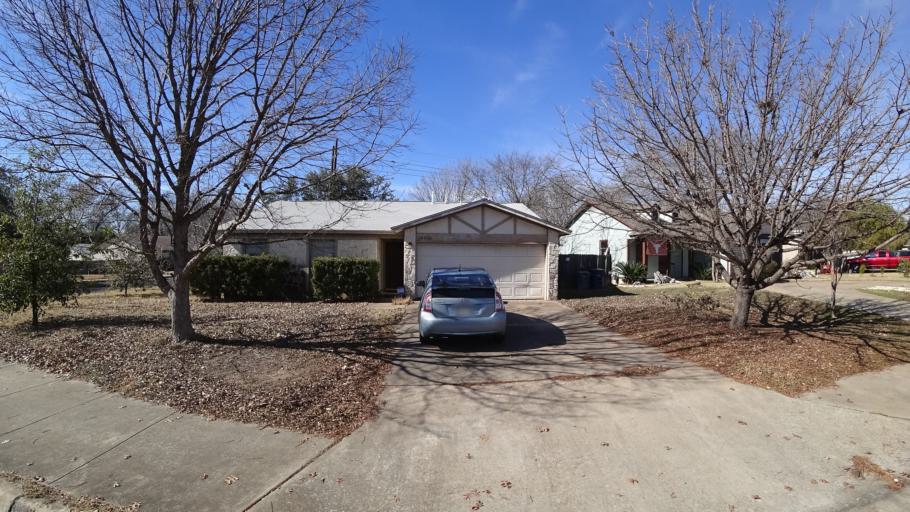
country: US
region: Texas
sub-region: Travis County
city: Wells Branch
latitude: 30.3667
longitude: -97.6881
